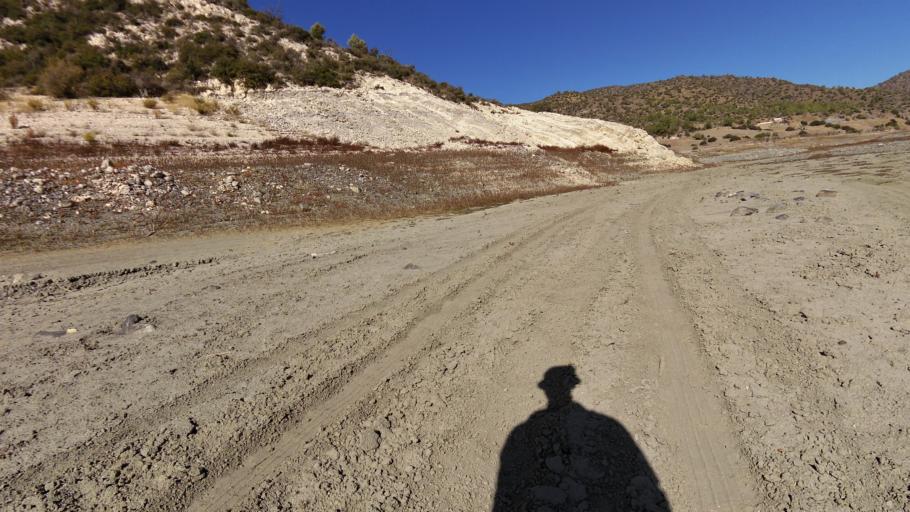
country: CY
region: Limassol
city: Mouttagiaka
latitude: 34.7569
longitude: 33.0912
